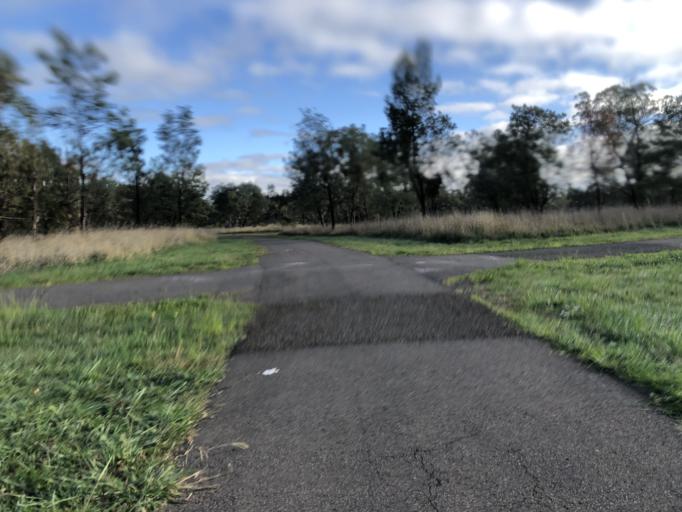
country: AU
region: New South Wales
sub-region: Orange Municipality
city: Orange
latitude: -33.3266
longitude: 149.0871
